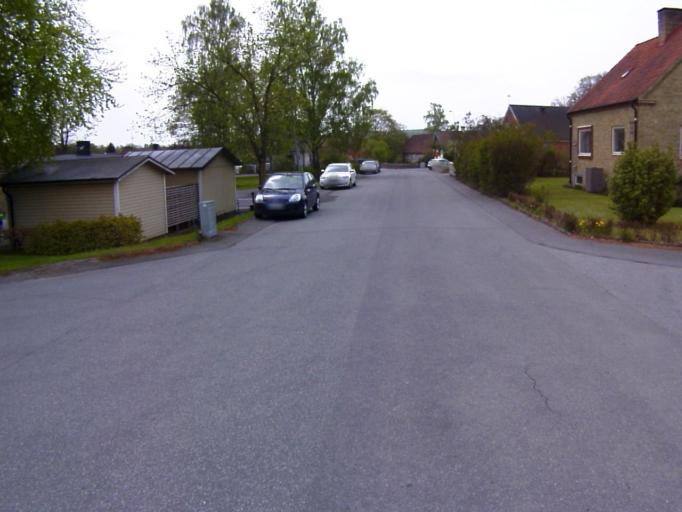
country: SE
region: Skane
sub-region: Kristianstads Kommun
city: Onnestad
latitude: 55.9333
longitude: 13.9872
